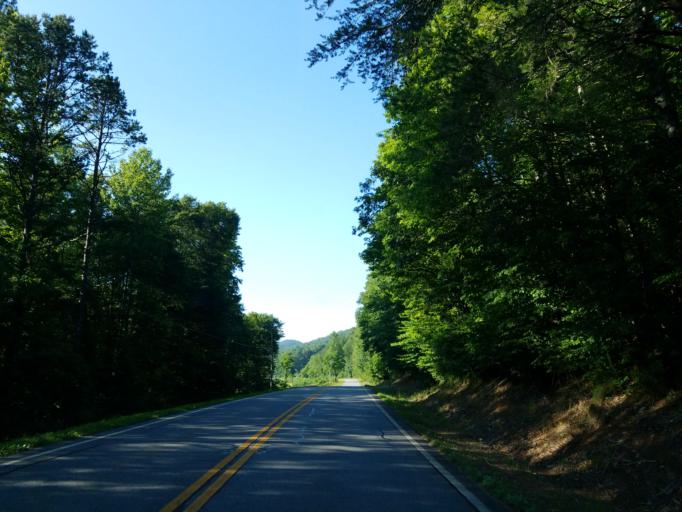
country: US
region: Georgia
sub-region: Fannin County
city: Blue Ridge
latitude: 34.7841
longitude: -84.1849
